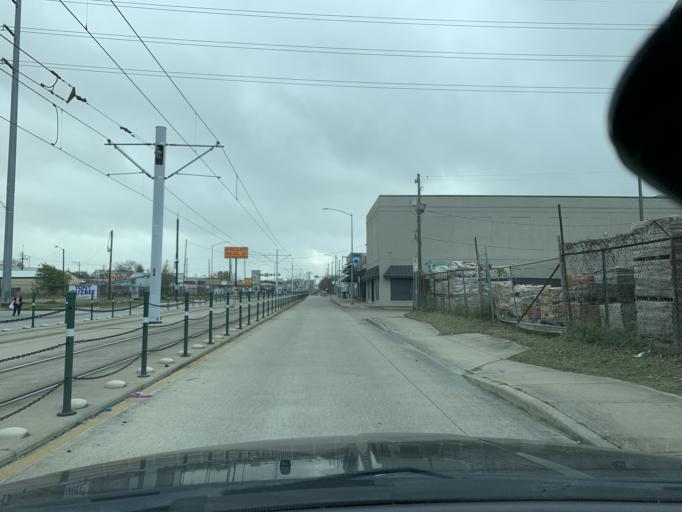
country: US
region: Texas
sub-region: Harris County
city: Houston
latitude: 29.7777
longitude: -95.3624
